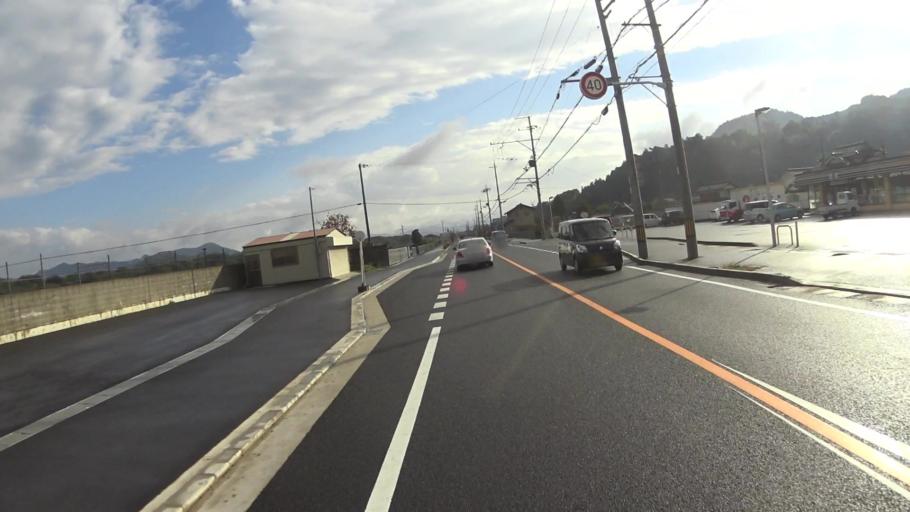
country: JP
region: Kyoto
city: Ayabe
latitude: 35.3039
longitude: 135.2049
